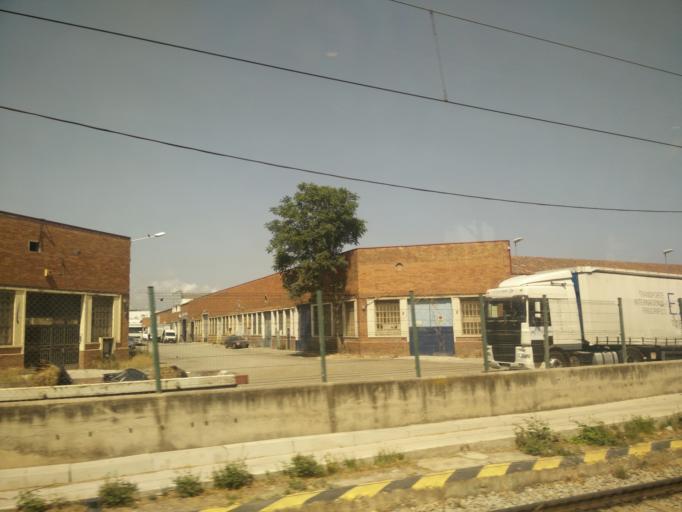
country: ES
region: Catalonia
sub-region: Provincia de Barcelona
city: Sant Adria de Besos
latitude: 41.4281
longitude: 2.2065
